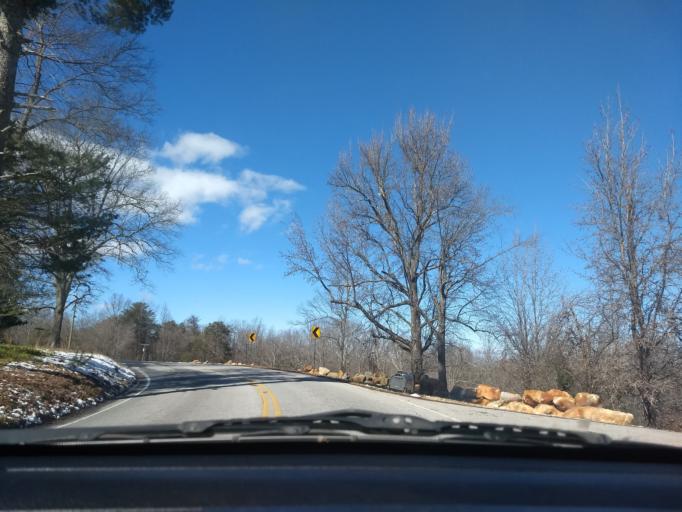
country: US
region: South Carolina
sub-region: Greenville County
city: Greenville
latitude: 34.8973
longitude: -82.3800
